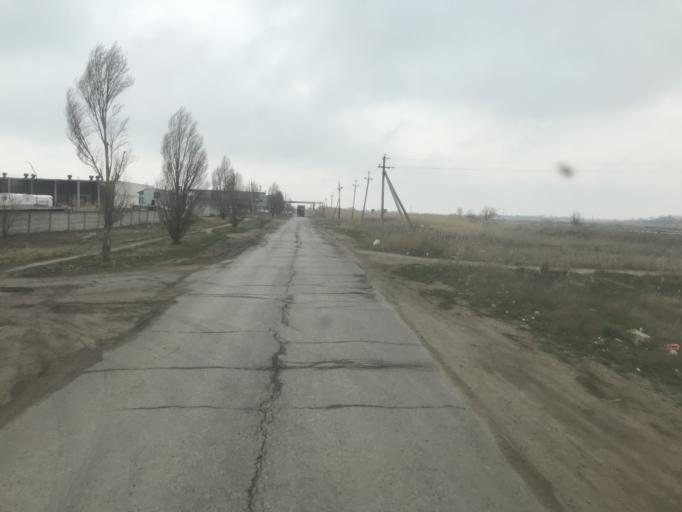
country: RU
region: Volgograd
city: Svetlyy Yar
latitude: 48.5235
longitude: 44.6190
